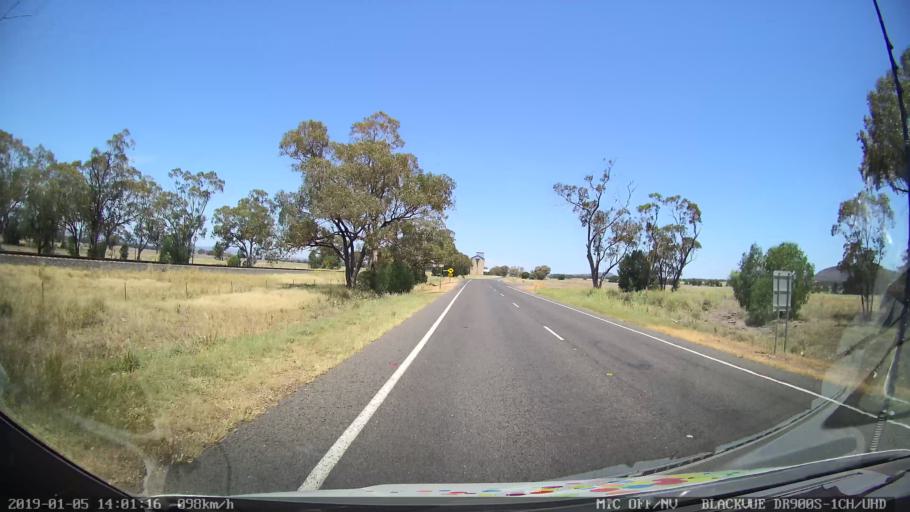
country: AU
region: New South Wales
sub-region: Gunnedah
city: Gunnedah
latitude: -31.1680
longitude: 150.3230
